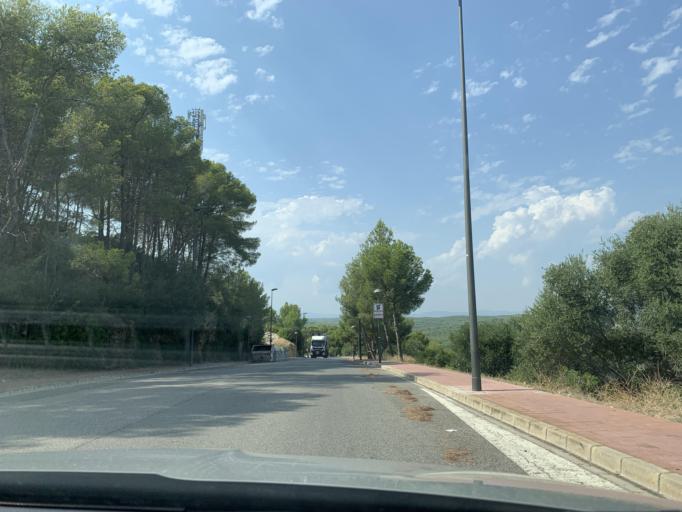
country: ES
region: Catalonia
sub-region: Provincia de Tarragona
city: Altafulla
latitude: 41.1341
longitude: 1.3552
